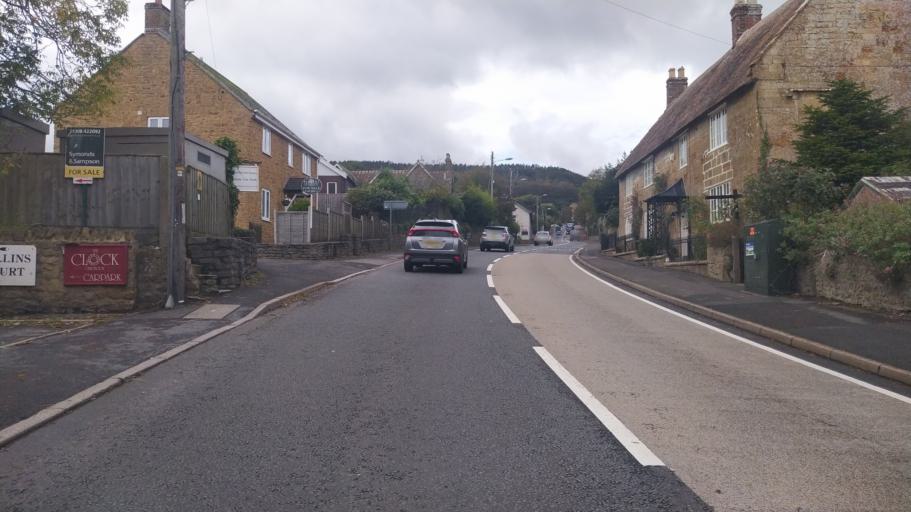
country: GB
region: England
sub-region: Dorset
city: Bridport
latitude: 50.7325
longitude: -2.8219
